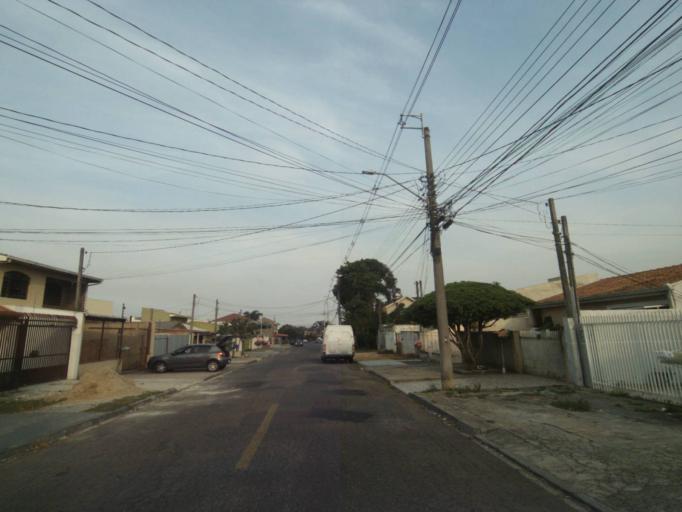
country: BR
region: Parana
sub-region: Pinhais
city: Pinhais
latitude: -25.4854
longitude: -49.2028
